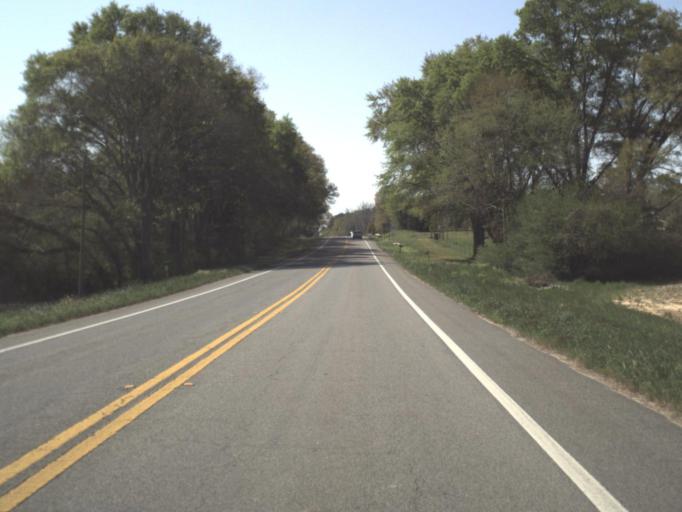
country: US
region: Florida
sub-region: Washington County
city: Chipley
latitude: 30.8413
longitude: -85.5009
